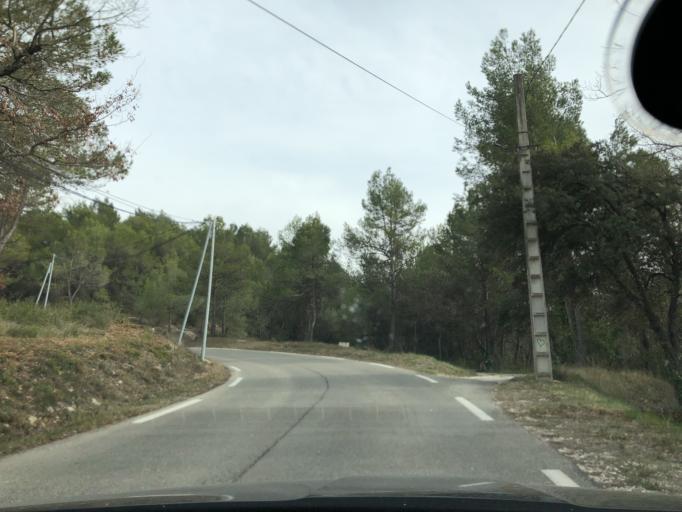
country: FR
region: Provence-Alpes-Cote d'Azur
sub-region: Departement du Vaucluse
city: Menerbes
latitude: 43.8447
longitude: 5.2243
